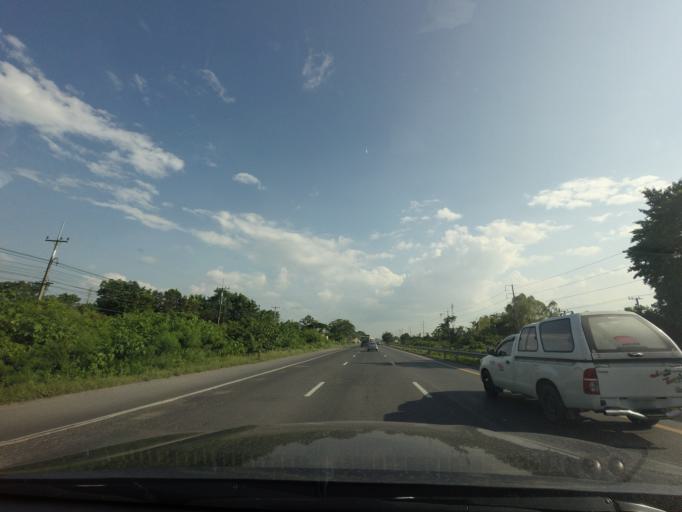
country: TH
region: Sara Buri
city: Chaloem Phra Kiat
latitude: 14.6254
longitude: 100.8904
